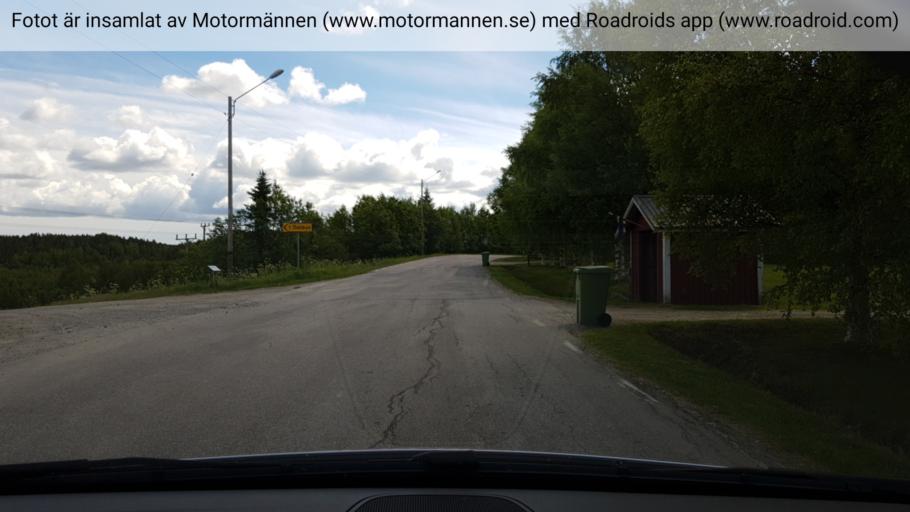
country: SE
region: Vaesterbotten
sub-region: Umea Kommun
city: Roback
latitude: 64.0330
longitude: 20.0824
